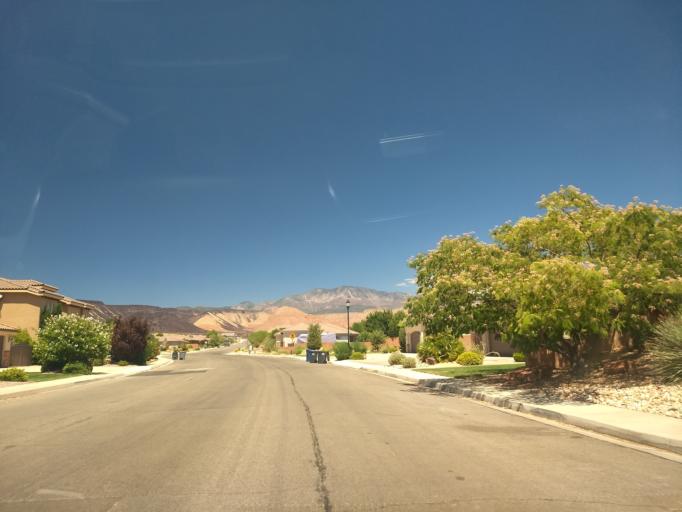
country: US
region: Utah
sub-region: Washington County
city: Washington
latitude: 37.1523
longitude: -113.5214
